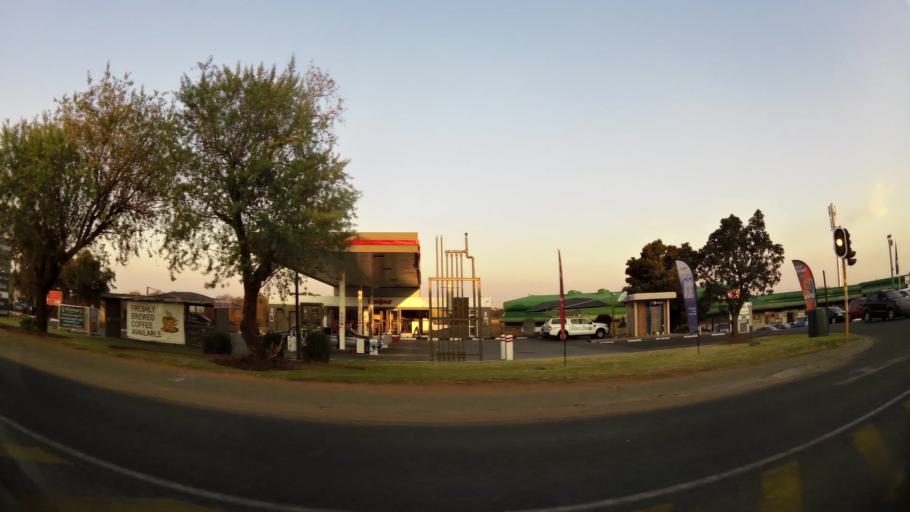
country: ZA
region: Gauteng
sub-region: City of Johannesburg Metropolitan Municipality
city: Modderfontein
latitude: -26.0808
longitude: 28.2202
